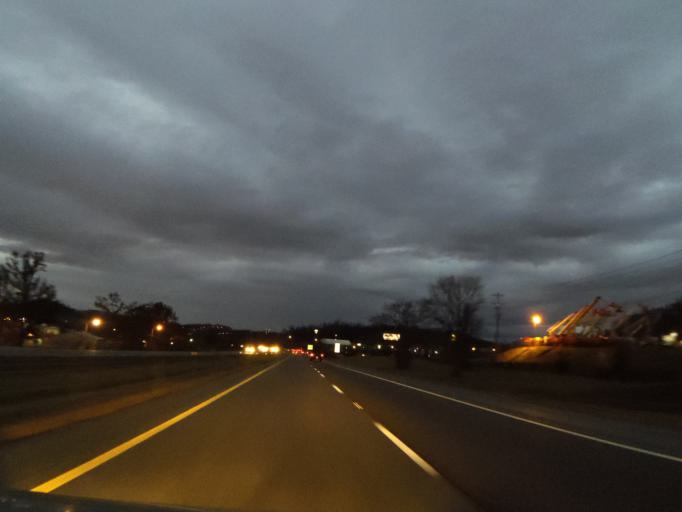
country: US
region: Tennessee
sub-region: Sullivan County
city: Colonial Heights
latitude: 36.4428
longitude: -82.5222
